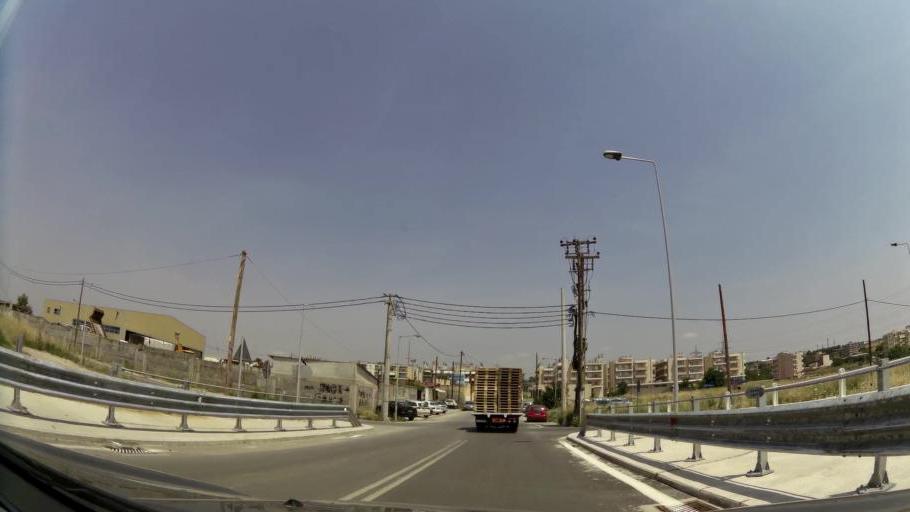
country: GR
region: Central Macedonia
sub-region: Nomos Thessalonikis
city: Evosmos
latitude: 40.6784
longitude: 22.8984
